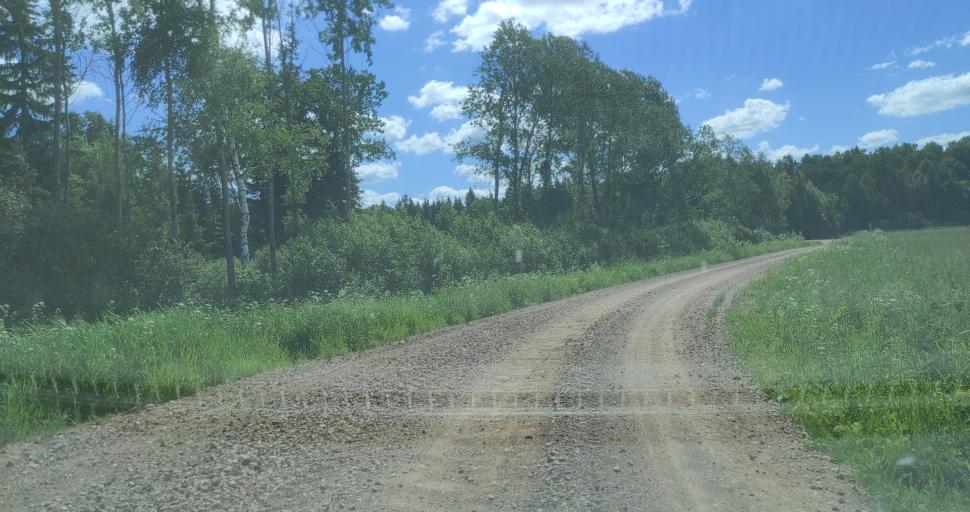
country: LV
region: Aizpute
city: Aizpute
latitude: 56.8427
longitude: 21.7132
